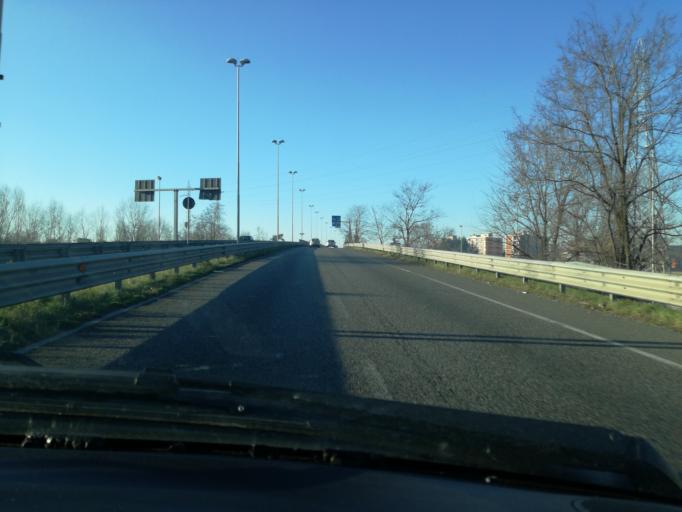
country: IT
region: Lombardy
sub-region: Provincia di Monza e Brianza
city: Monza
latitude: 45.5632
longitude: 9.2763
